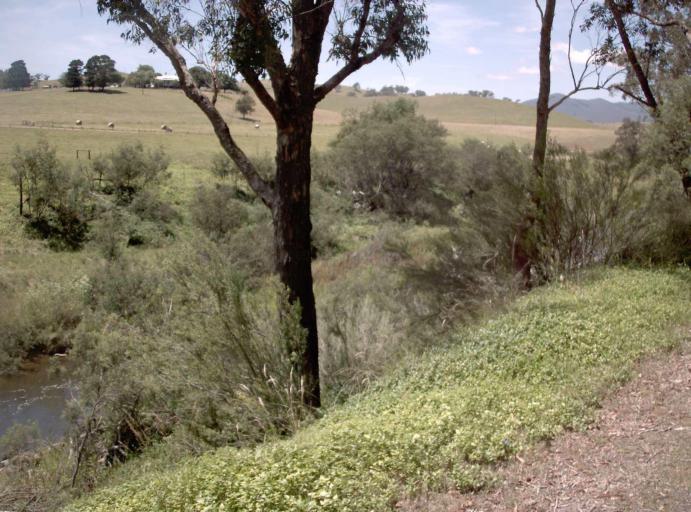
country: AU
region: Victoria
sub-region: East Gippsland
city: Bairnsdale
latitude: -37.3969
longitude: 147.8332
